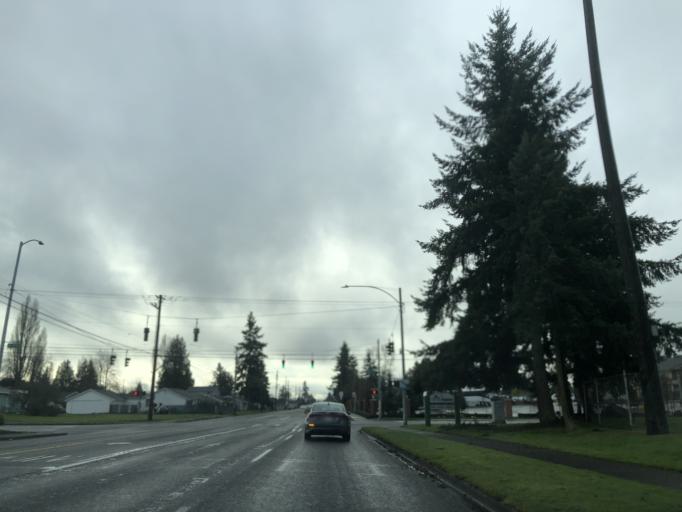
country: US
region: Washington
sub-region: Pierce County
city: Tacoma
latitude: 47.2472
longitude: -122.4630
